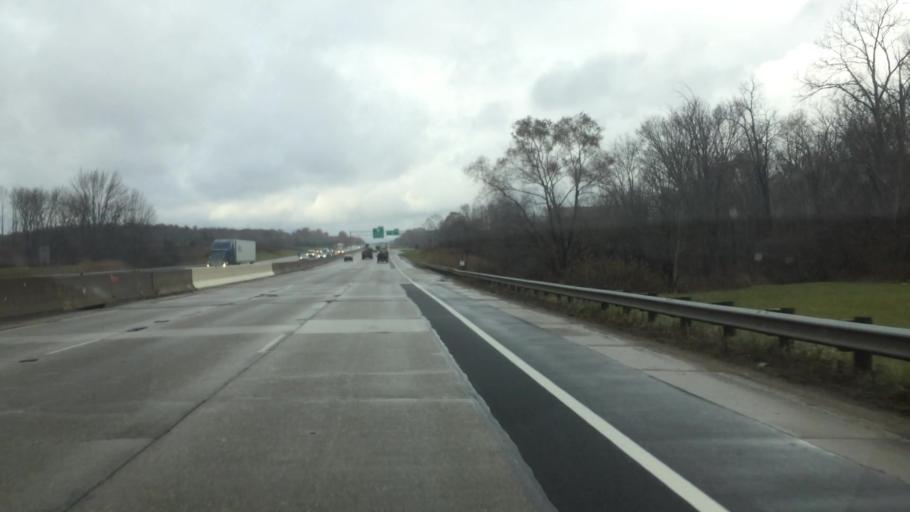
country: US
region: Ohio
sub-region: Summit County
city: Silver Lake
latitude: 41.1957
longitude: -81.4796
